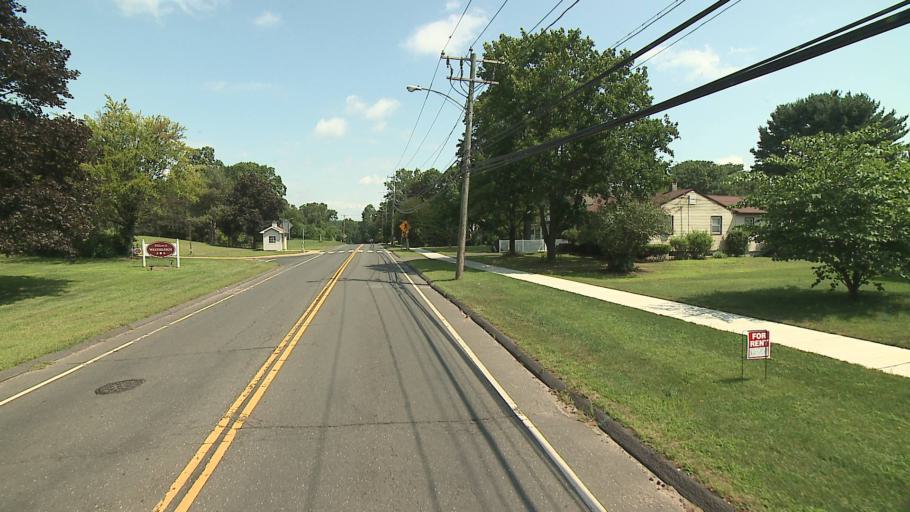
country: US
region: Connecticut
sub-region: Hartford County
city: Farmington
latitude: 41.7475
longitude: -72.8870
